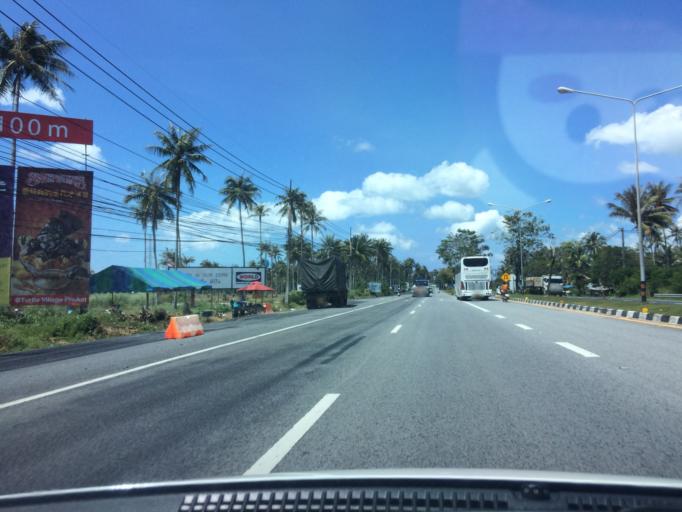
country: TH
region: Phuket
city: Thalang
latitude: 8.1662
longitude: 98.3026
